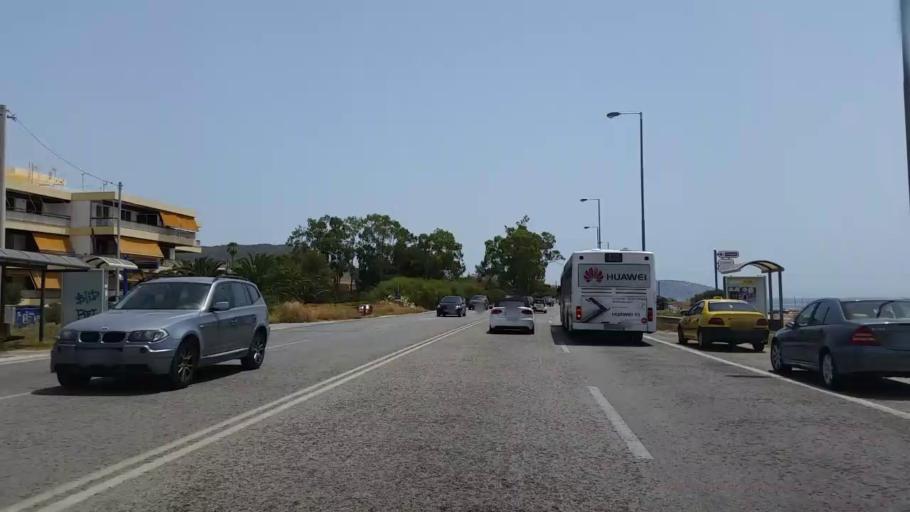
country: GR
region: Attica
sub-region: Nomarchia Anatolikis Attikis
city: Saronida
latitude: 37.7568
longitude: 23.9025
